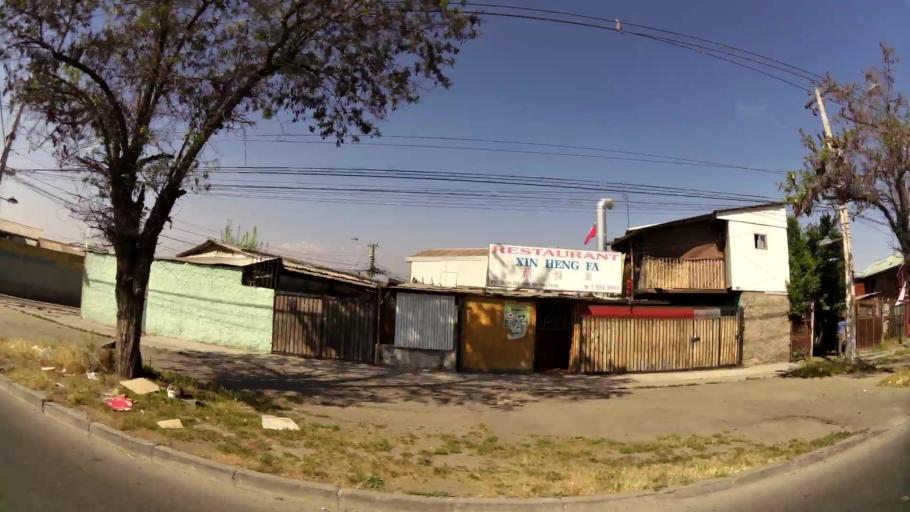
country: CL
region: Santiago Metropolitan
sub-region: Provincia de Santiago
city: La Pintana
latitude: -33.5294
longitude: -70.6098
